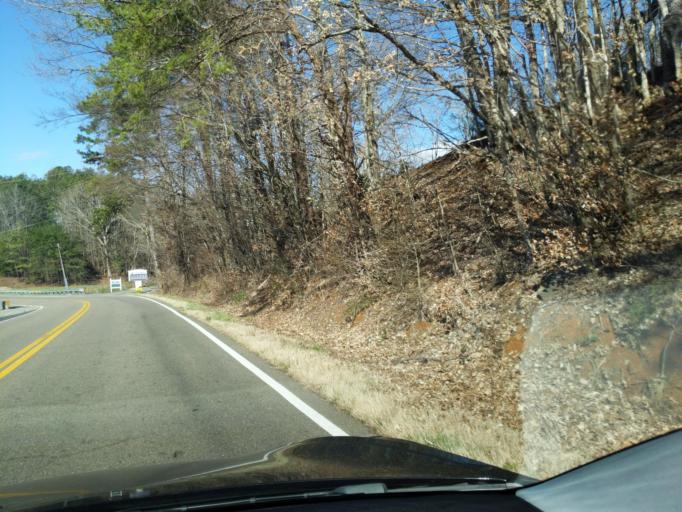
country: US
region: Tennessee
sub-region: Jefferson County
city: Dandridge
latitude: 35.9783
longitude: -83.4831
